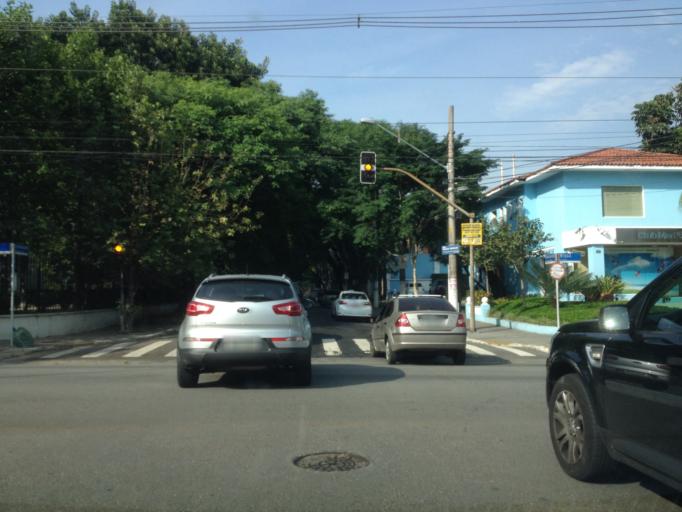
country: BR
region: Sao Paulo
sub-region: Sao Paulo
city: Sao Paulo
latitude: -23.5755
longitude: -46.6654
